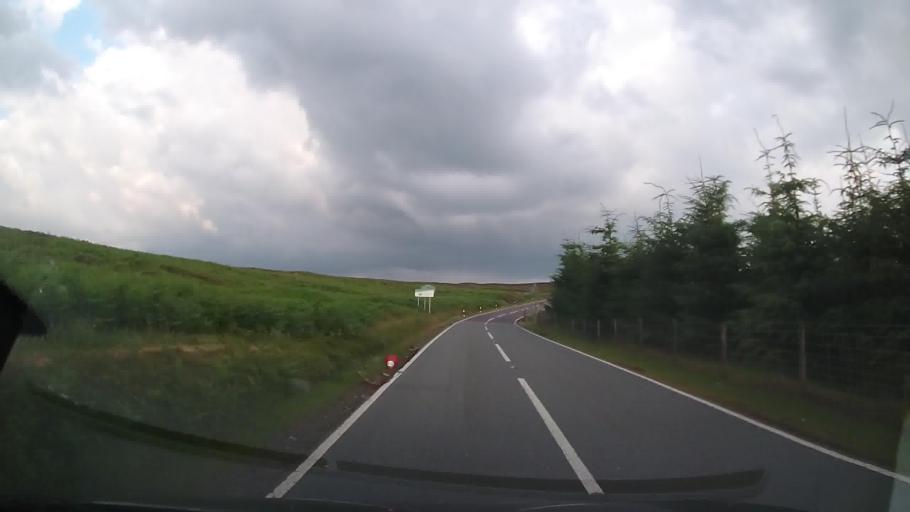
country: GB
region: Wales
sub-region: Denbighshire
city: Llandrillo
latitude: 52.8958
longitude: -3.4897
